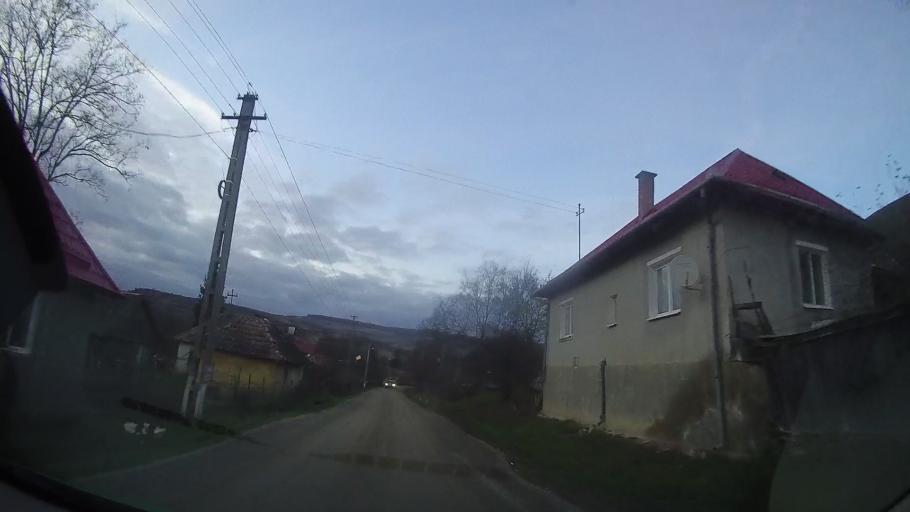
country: RO
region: Cluj
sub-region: Comuna Palatca
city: Palatca
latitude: 46.8676
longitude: 24.0154
